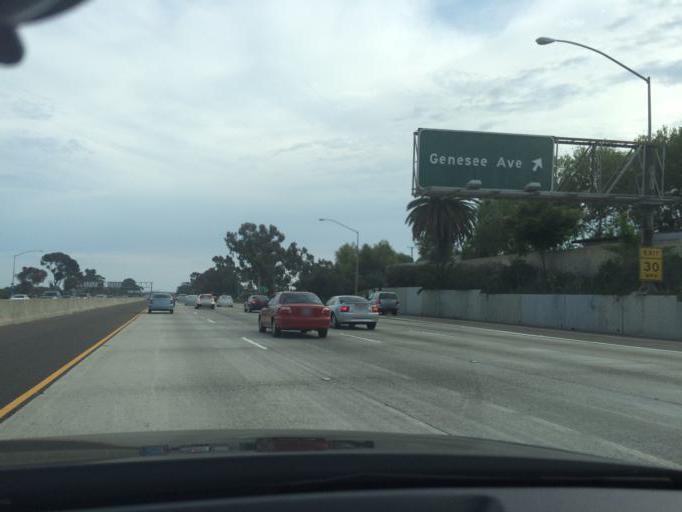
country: US
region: California
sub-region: San Diego County
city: San Diego
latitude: 32.7945
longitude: -117.1581
